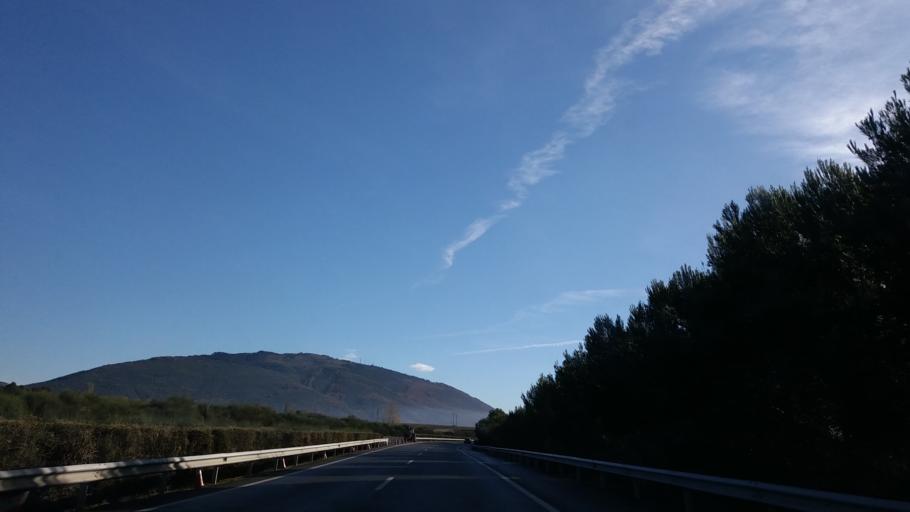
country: ES
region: Navarre
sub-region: Provincia de Navarra
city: Berriobeiti
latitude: 42.8540
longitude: -1.7181
